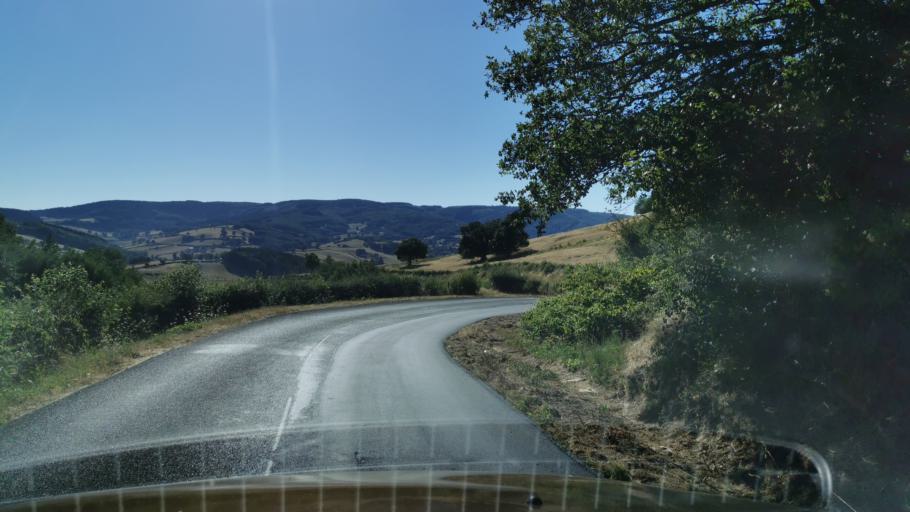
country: FR
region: Bourgogne
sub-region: Departement de Saone-et-Loire
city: Marmagne
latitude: 46.8030
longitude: 4.3523
